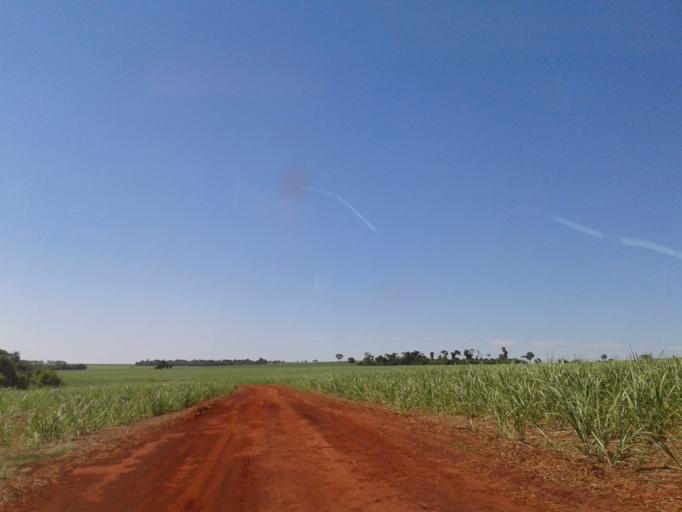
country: BR
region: Minas Gerais
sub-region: Centralina
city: Centralina
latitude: -18.6310
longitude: -49.2595
